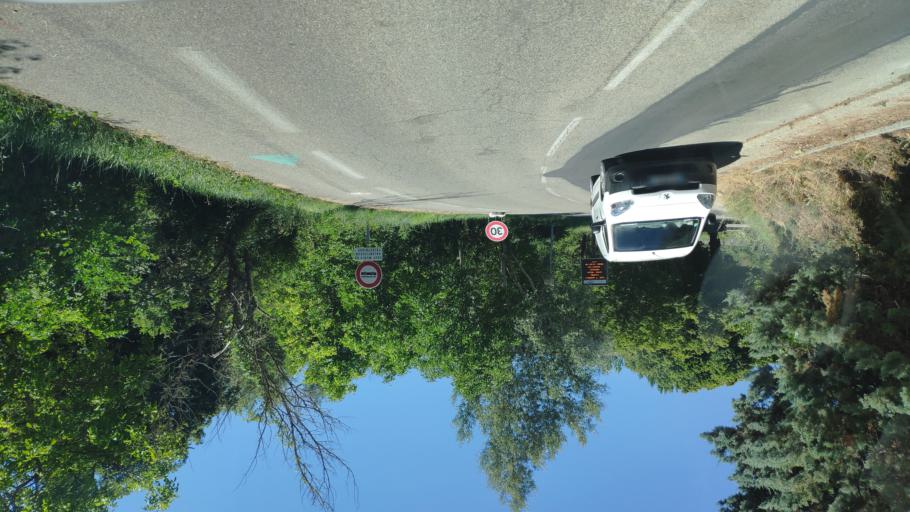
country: FR
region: Provence-Alpes-Cote d'Azur
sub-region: Departement du Vaucluse
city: Malaucene
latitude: 44.1710
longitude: 5.1395
